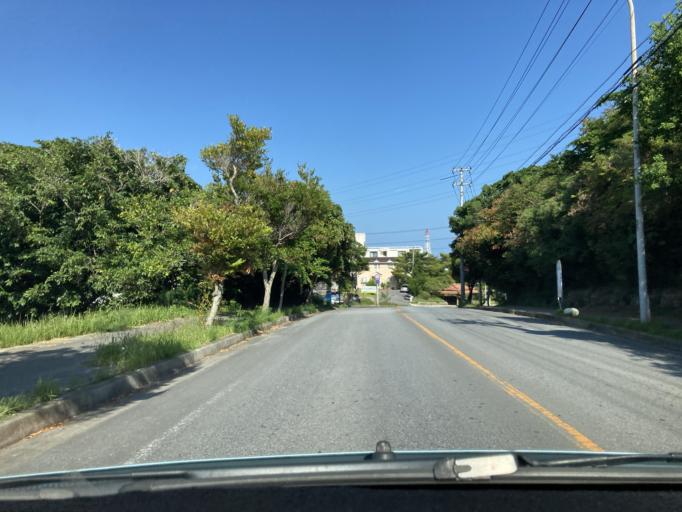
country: JP
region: Okinawa
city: Ginowan
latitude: 26.2551
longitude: 127.7242
